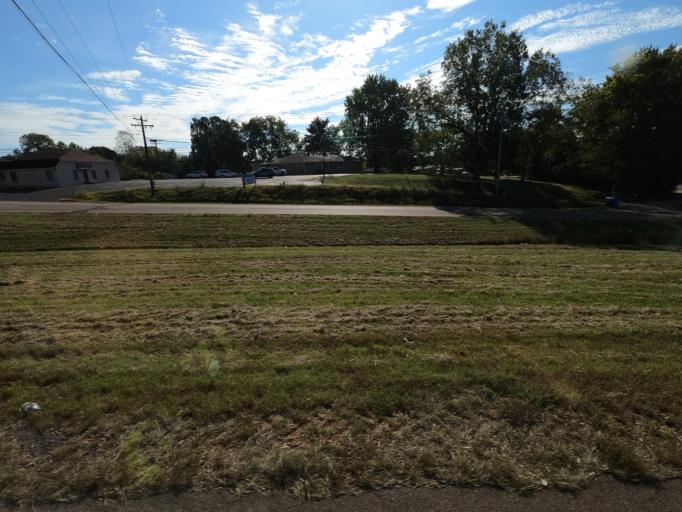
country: US
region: Tennessee
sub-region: Tipton County
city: Munford
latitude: 35.4208
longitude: -89.8198
